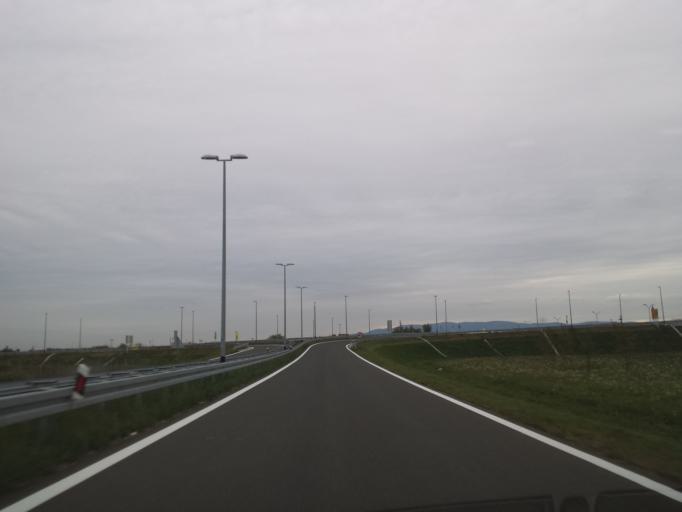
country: HR
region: Grad Zagreb
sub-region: Sesvete
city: Sesvete
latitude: 45.7906
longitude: 16.1659
